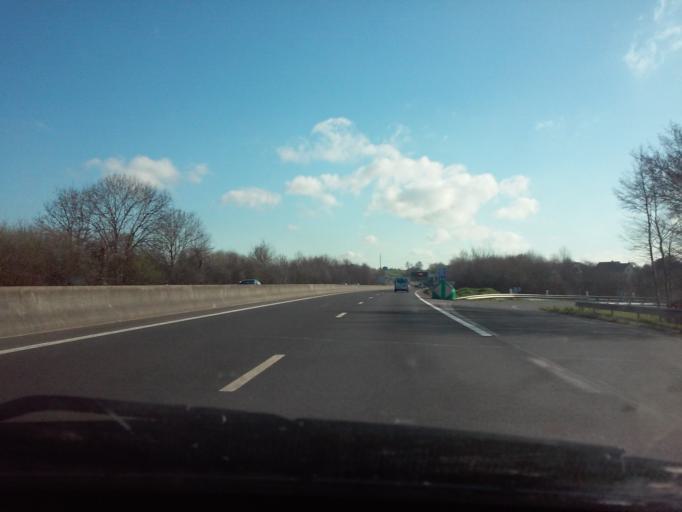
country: FR
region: Lower Normandy
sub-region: Departement de la Manche
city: Saint-Senier-sous-Avranches
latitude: 48.7017
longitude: -1.3442
